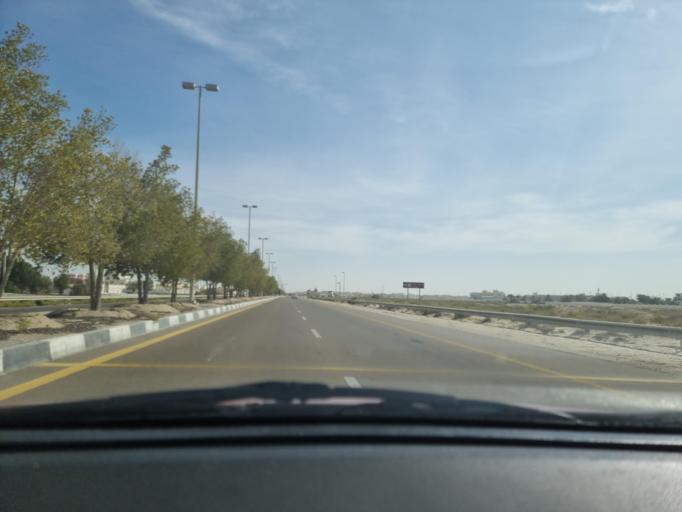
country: AE
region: Abu Dhabi
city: Abu Dhabi
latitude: 24.3827
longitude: 54.6852
